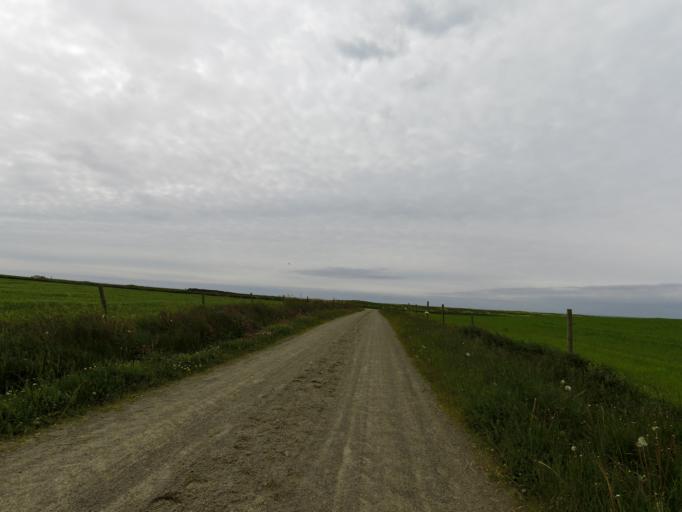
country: NO
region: Rogaland
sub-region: Ha
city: Naerbo
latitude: 58.6765
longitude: 5.5487
